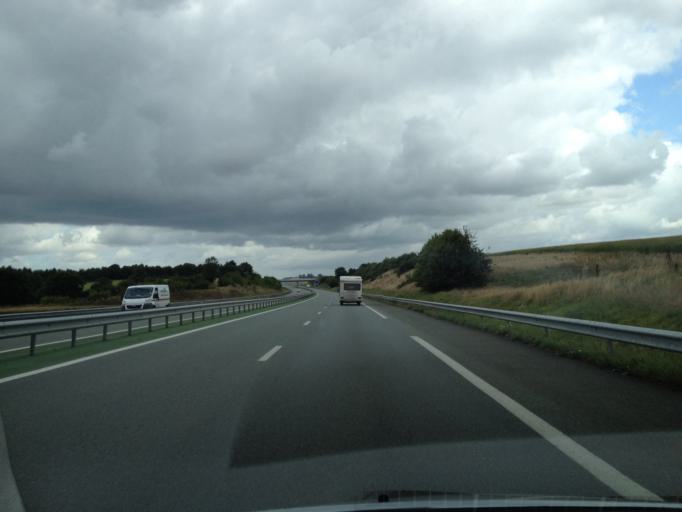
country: FR
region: Pays de la Loire
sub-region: Departement de Maine-et-Loire
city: Nuaille
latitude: 47.1188
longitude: -0.8253
